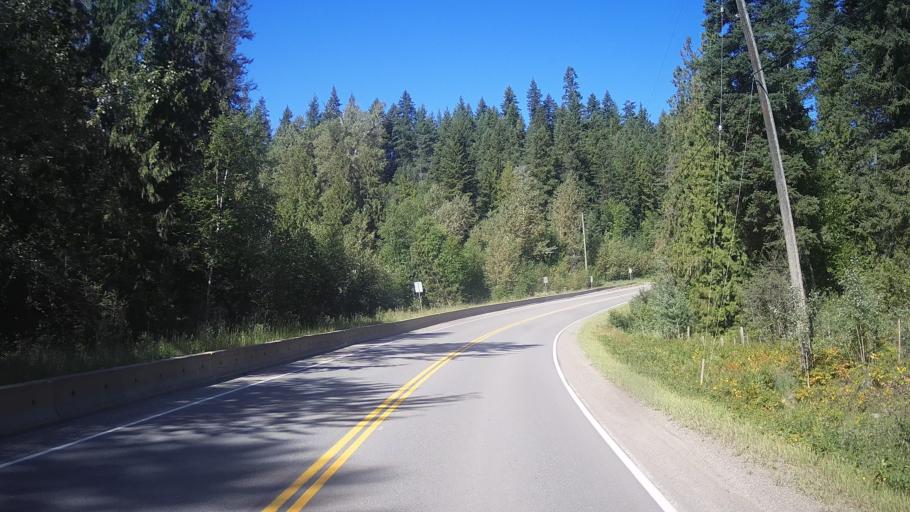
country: CA
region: British Columbia
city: Kamloops
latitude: 51.4536
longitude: -120.2205
